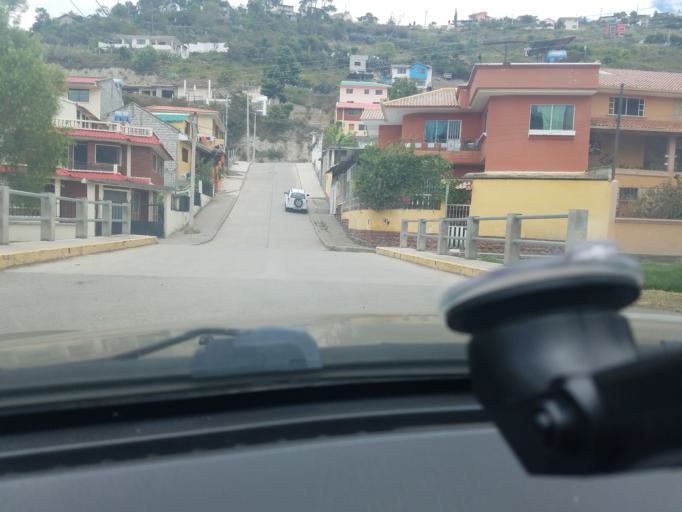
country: EC
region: Azuay
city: La Union
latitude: -2.7806
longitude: -78.7633
